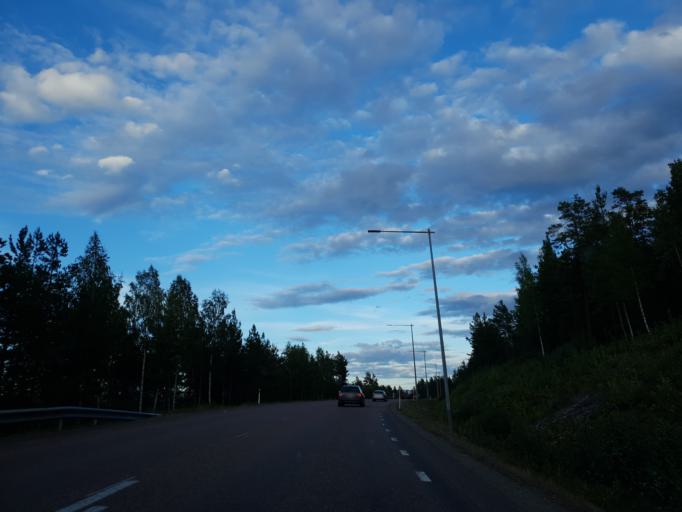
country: SE
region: Gaevleborg
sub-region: Soderhamns Kommun
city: Soderhamn
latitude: 61.2922
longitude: 17.0564
